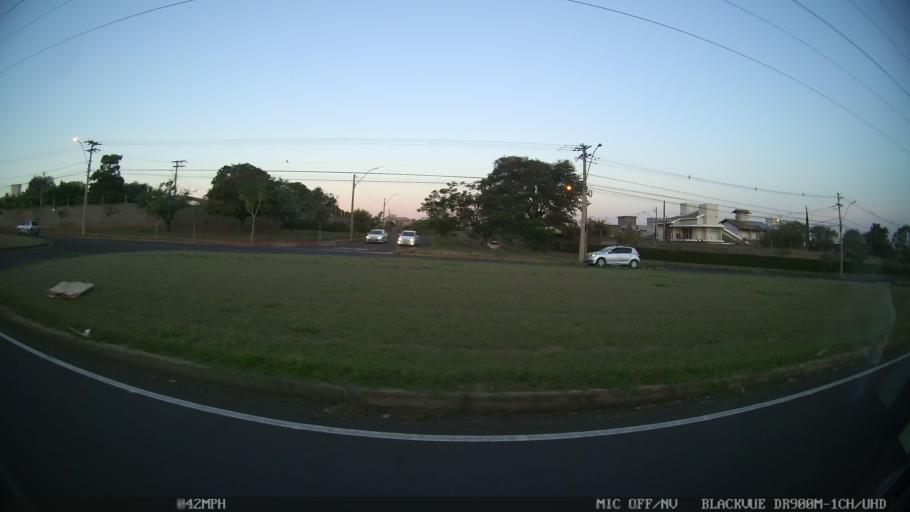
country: BR
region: Sao Paulo
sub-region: Sao Jose Do Rio Preto
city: Sao Jose do Rio Preto
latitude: -20.8202
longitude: -49.3399
